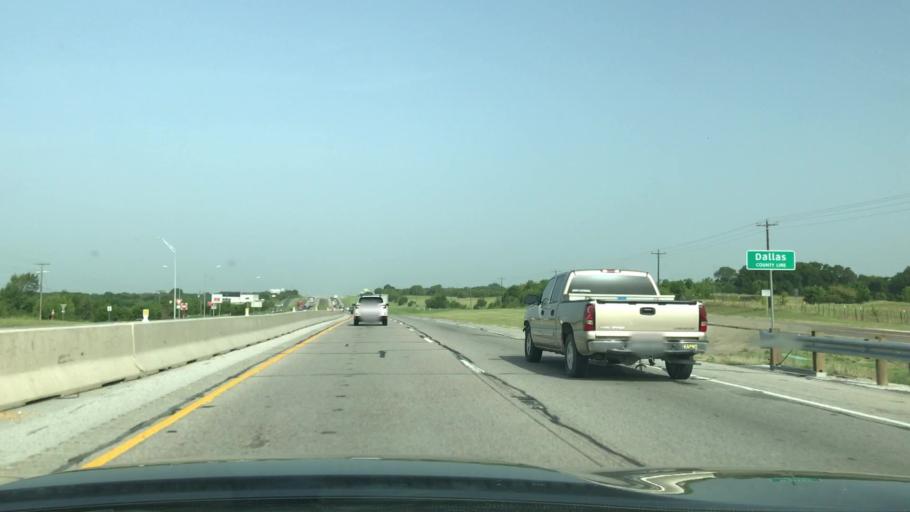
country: US
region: Texas
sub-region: Dallas County
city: Sunnyvale
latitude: 32.7777
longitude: -96.5193
